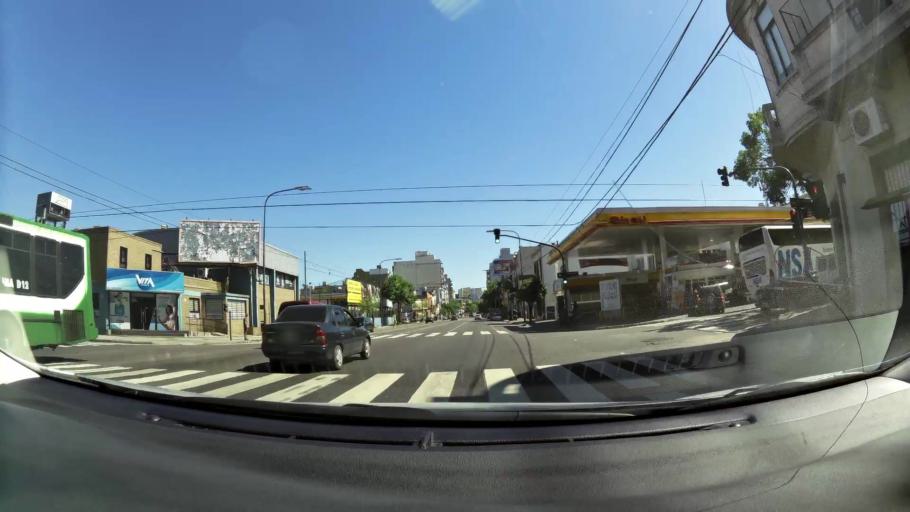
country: AR
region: Buenos Aires F.D.
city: Buenos Aires
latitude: -34.6306
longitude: -58.3908
